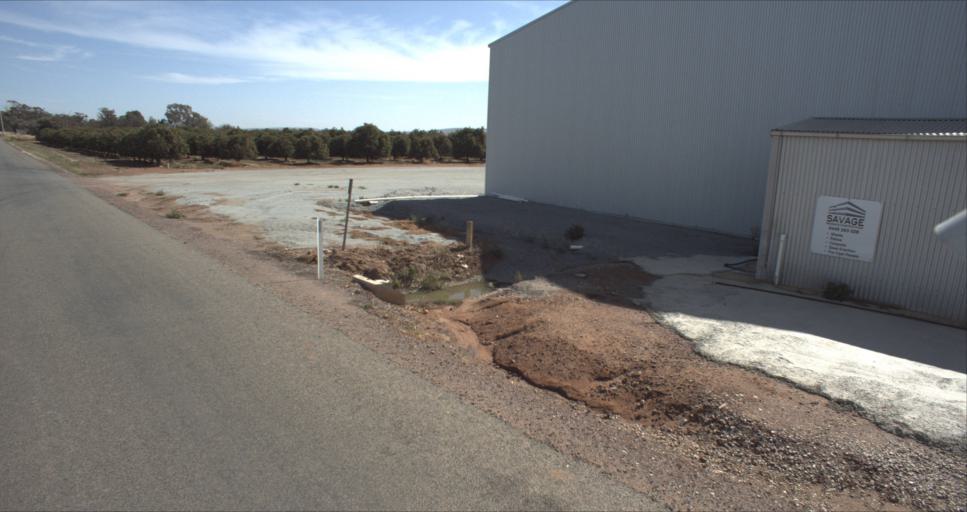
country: AU
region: New South Wales
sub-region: Leeton
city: Leeton
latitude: -34.5798
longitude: 146.4687
